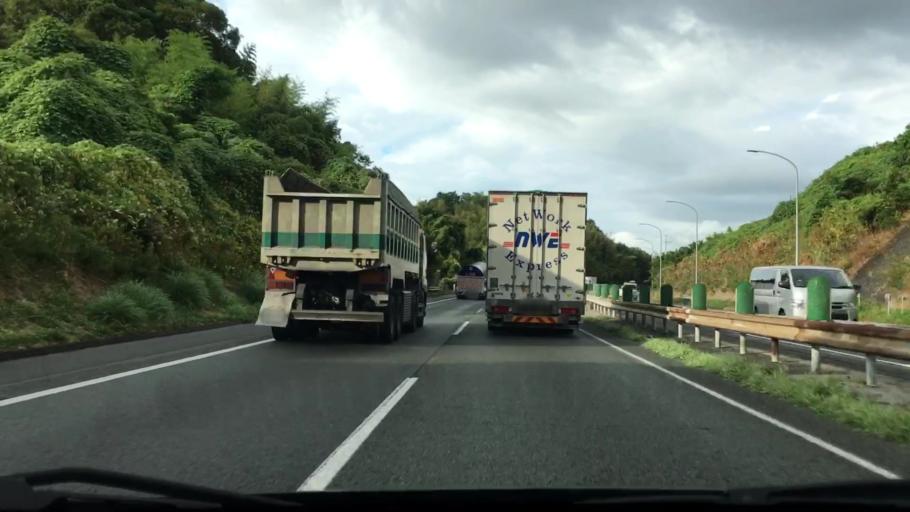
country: JP
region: Fukuoka
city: Nishifukuma
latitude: 33.7460
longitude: 130.5273
